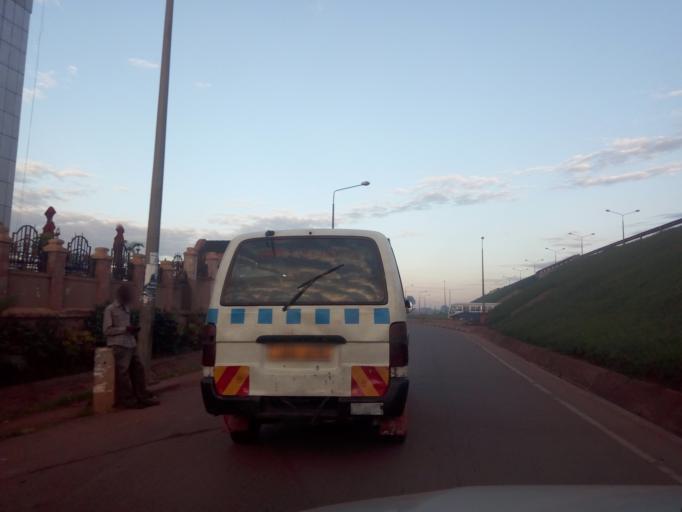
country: UG
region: Central Region
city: Kampala Central Division
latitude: 0.3494
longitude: 32.5641
